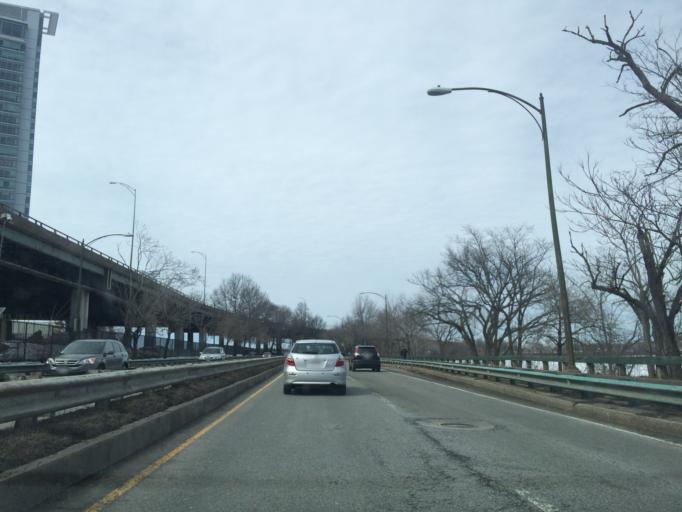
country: US
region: Massachusetts
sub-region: Norfolk County
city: Brookline
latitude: 42.3531
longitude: -71.1155
